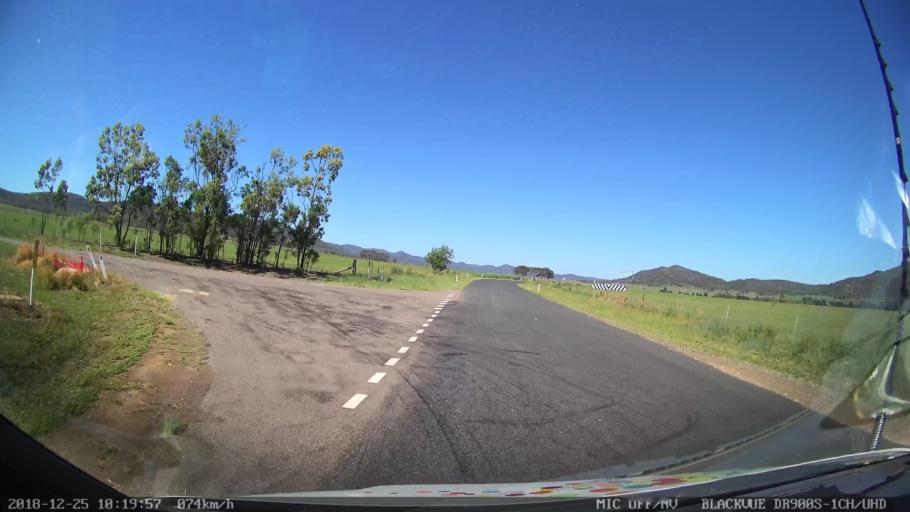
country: AU
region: New South Wales
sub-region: Muswellbrook
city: Denman
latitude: -32.3553
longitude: 150.5542
